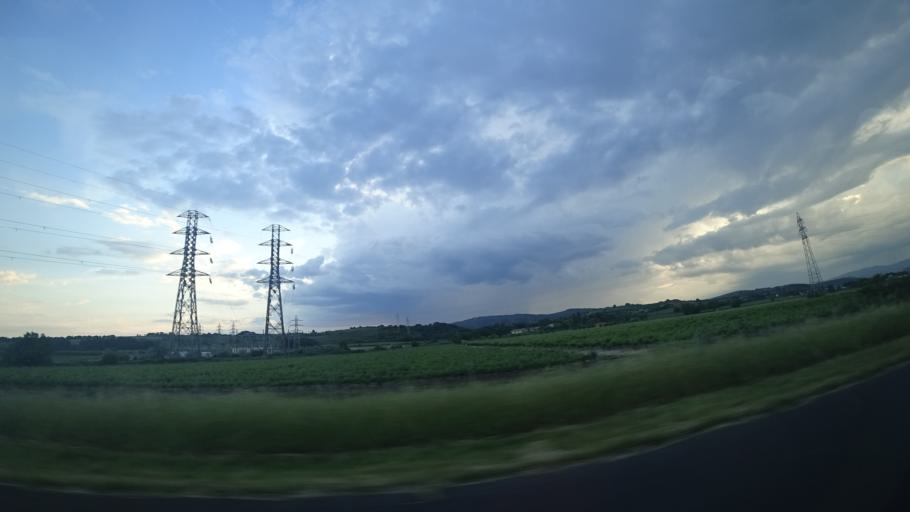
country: FR
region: Languedoc-Roussillon
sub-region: Departement de l'Herault
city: Nebian
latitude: 43.6078
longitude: 3.4611
